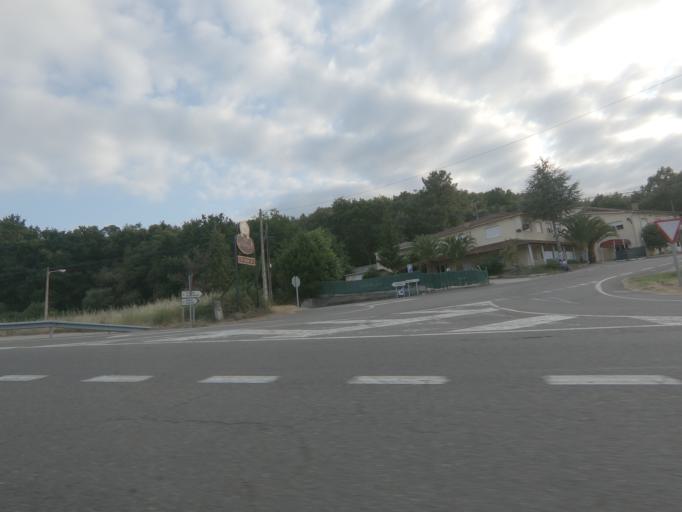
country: ES
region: Galicia
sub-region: Provincia de Ourense
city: Taboadela
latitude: 42.2360
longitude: -7.8455
